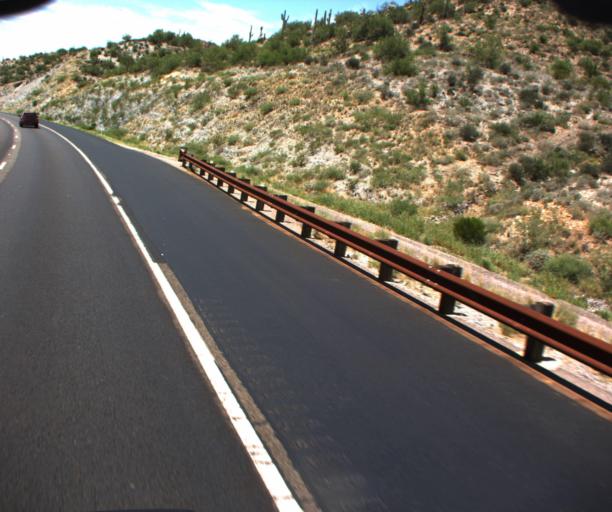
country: US
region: Arizona
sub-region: Pinal County
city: Gold Camp
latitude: 33.2767
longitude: -111.2314
